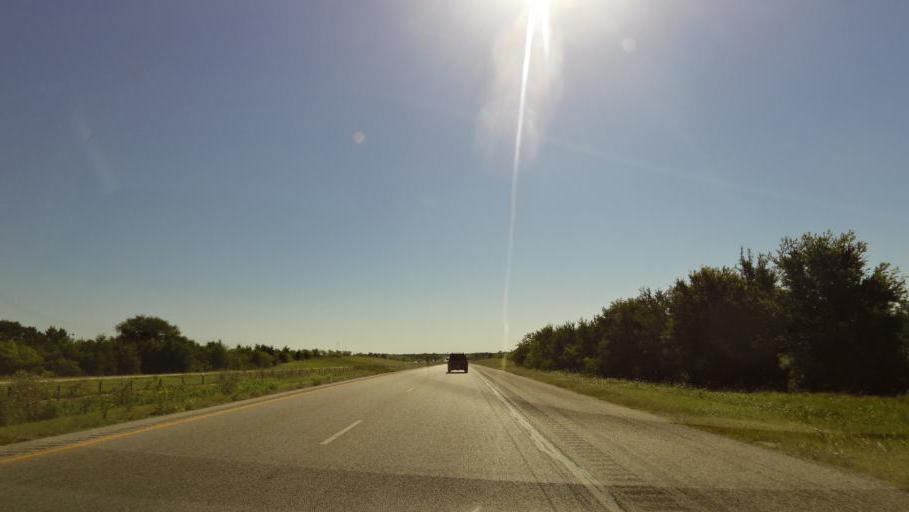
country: US
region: Texas
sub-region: Gonzales County
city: Waelder
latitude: 29.6666
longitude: -97.3319
